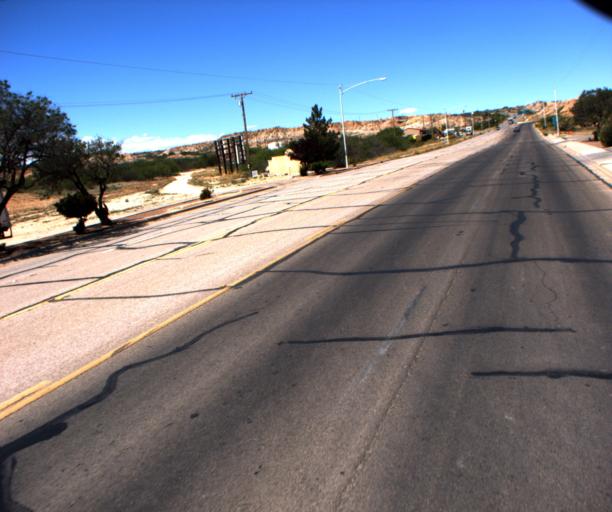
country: US
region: Arizona
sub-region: Cochise County
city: Benson
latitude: 31.9712
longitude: -110.3176
